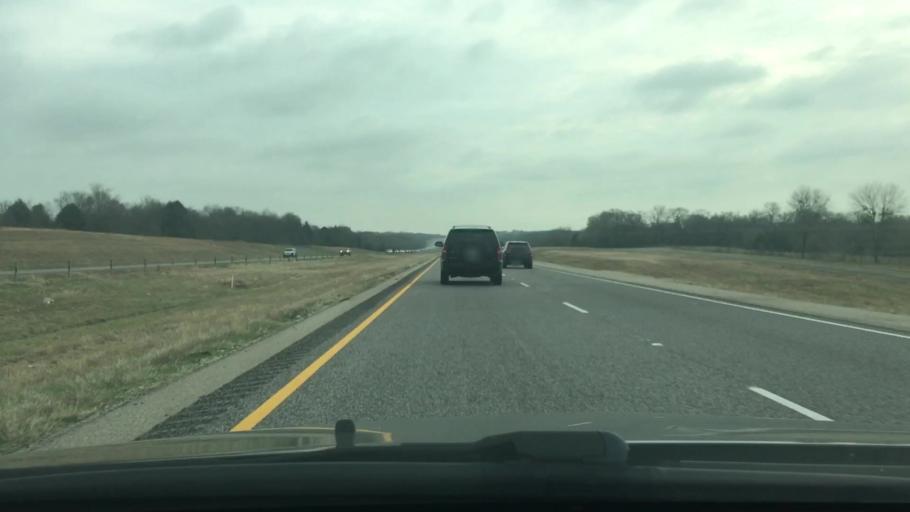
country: US
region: Texas
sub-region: Freestone County
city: Fairfield
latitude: 31.6622
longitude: -96.1621
